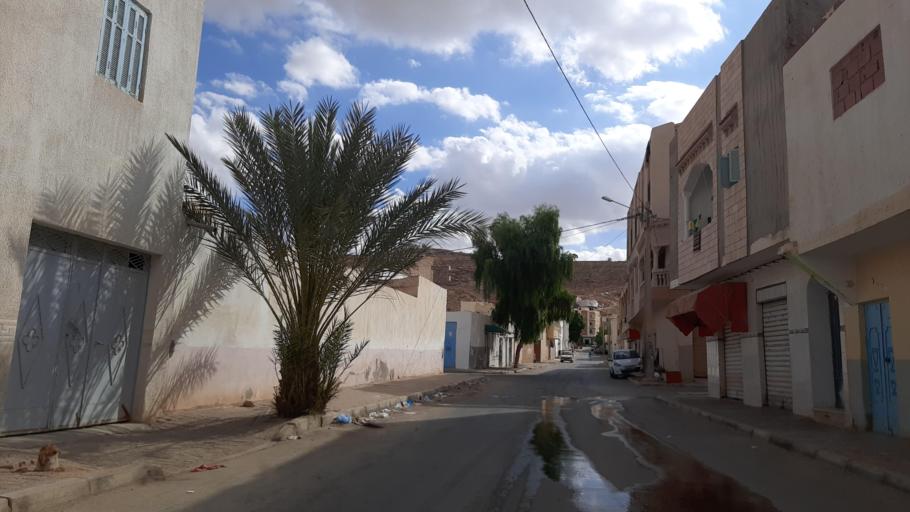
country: TN
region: Tataouine
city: Tataouine
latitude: 32.9278
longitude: 10.4556
